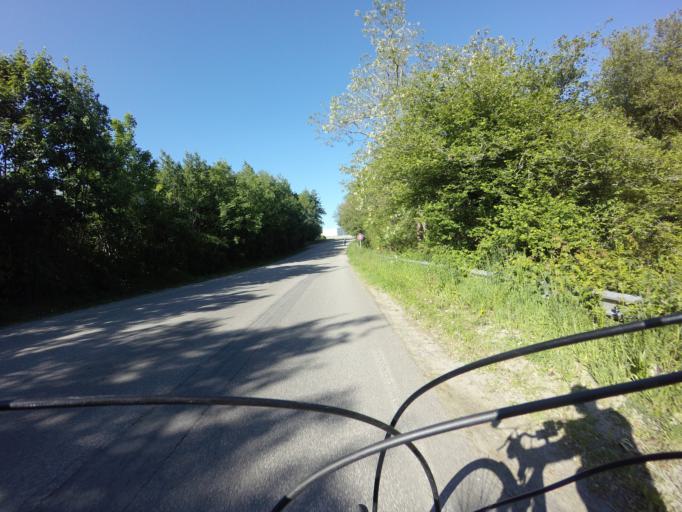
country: FR
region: Brittany
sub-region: Departement du Finistere
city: Plomelin
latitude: 47.9683
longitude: -4.1448
